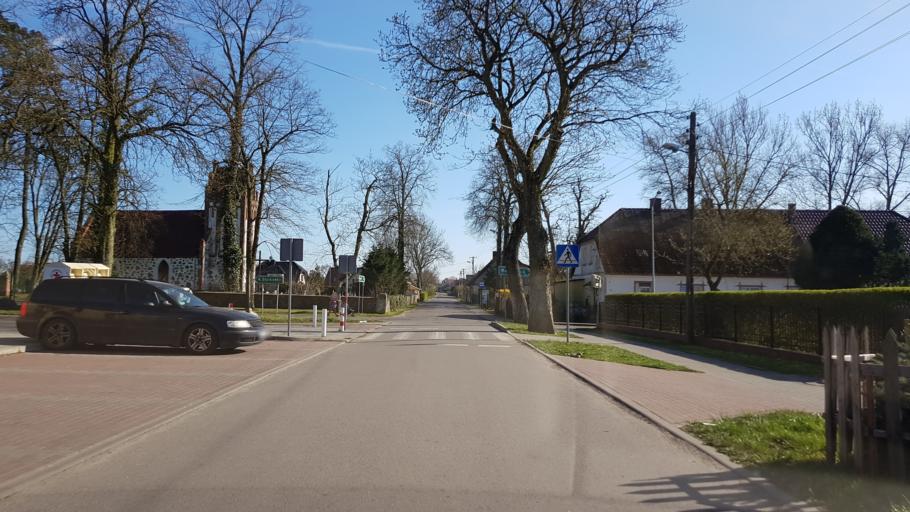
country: PL
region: West Pomeranian Voivodeship
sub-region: Powiat stargardzki
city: Stargard Szczecinski
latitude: 53.4061
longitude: 15.0284
